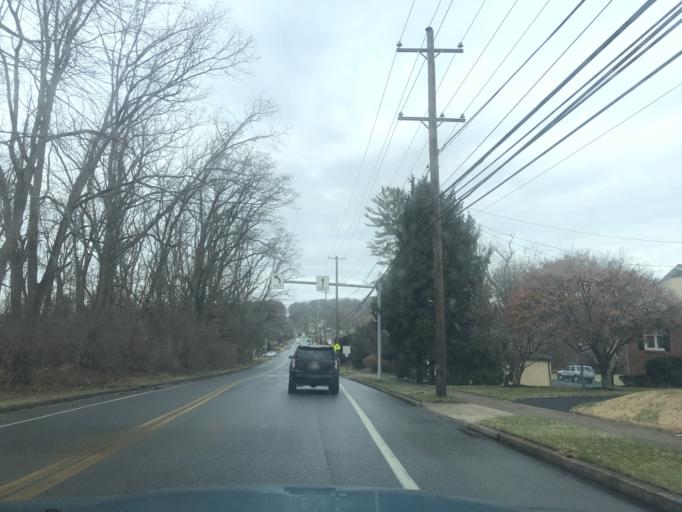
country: US
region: Pennsylvania
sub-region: Montgomery County
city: Dresher
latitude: 40.1278
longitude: -75.1450
